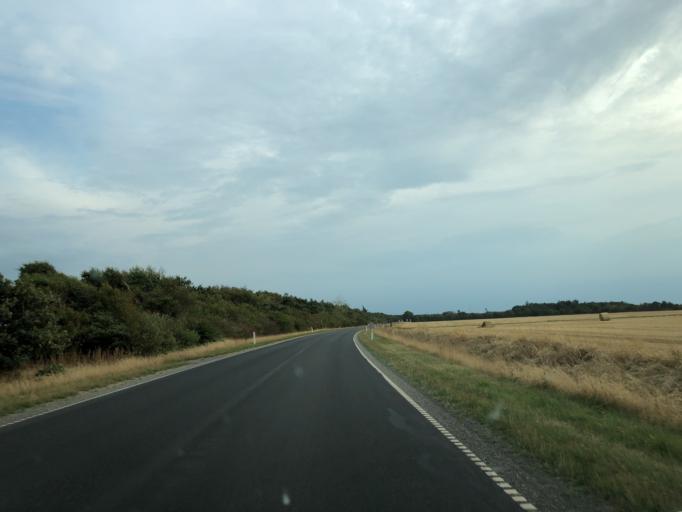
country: DK
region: Central Jutland
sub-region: Holstebro Kommune
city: Ulfborg
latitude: 56.3789
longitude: 8.4480
